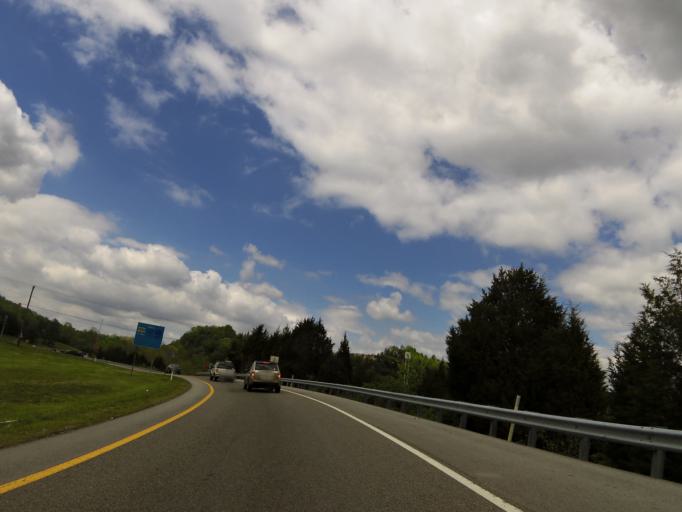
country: US
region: Tennessee
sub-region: Anderson County
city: Norris
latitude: 36.1075
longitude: -84.0221
